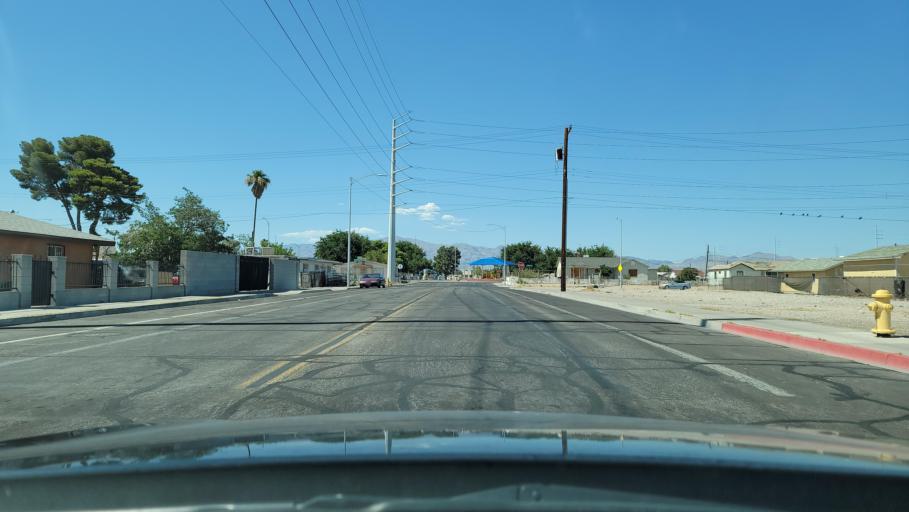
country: US
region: Nevada
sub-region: Clark County
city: Las Vegas
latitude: 36.1975
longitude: -115.1563
